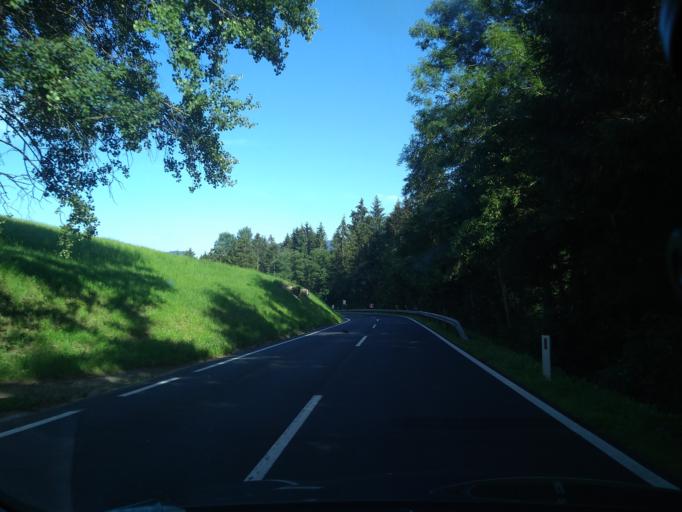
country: AT
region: Styria
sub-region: Politischer Bezirk Graz-Umgebung
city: Semriach
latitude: 47.2664
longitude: 15.4395
